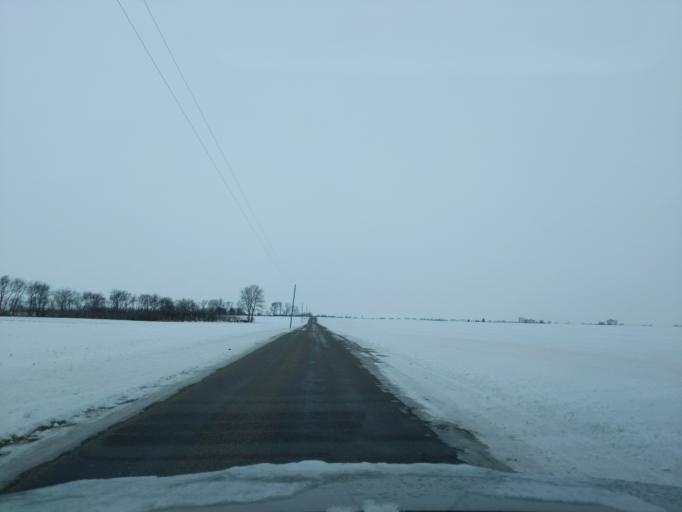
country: US
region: Indiana
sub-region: Benton County
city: Otterbein
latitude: 40.4553
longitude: -87.0928
